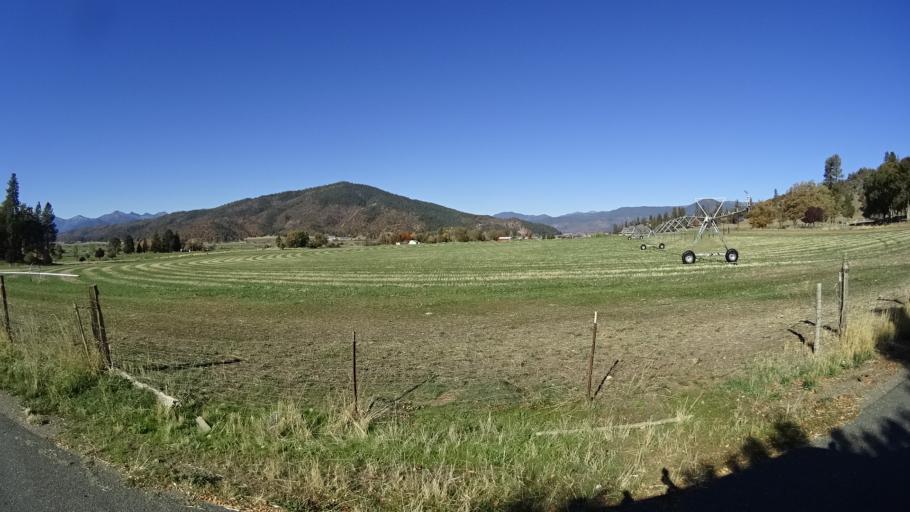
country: US
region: California
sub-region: Siskiyou County
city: Yreka
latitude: 41.5921
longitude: -122.8330
